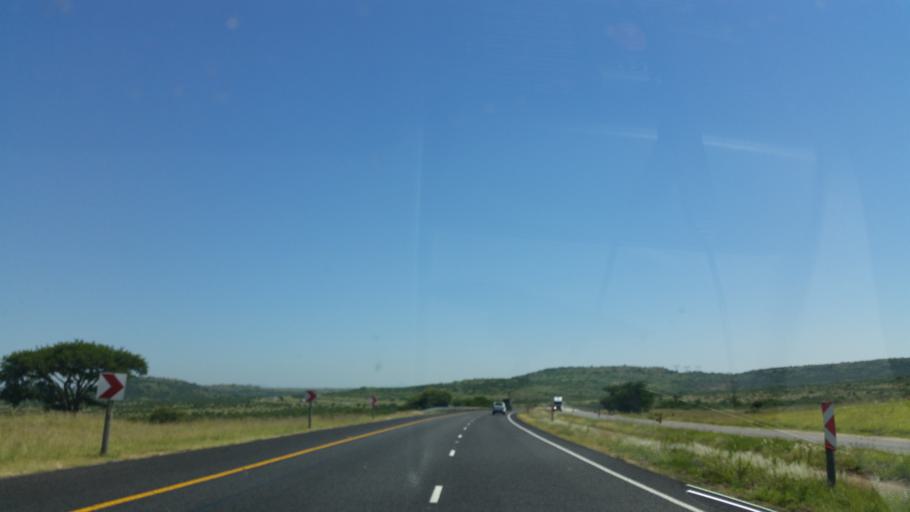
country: ZA
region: KwaZulu-Natal
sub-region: uThukela District Municipality
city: Ladysmith
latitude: -28.7031
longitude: 29.6398
